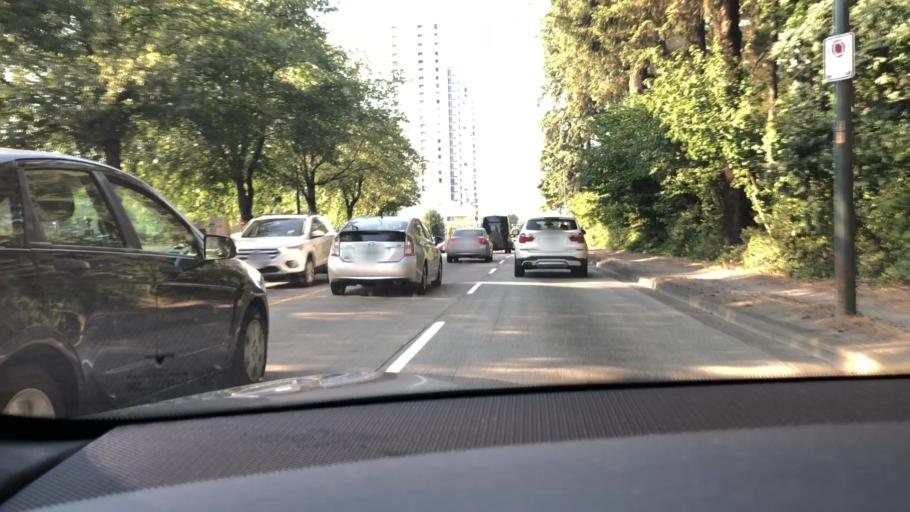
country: CA
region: British Columbia
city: Burnaby
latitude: 49.2305
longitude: -123.0235
